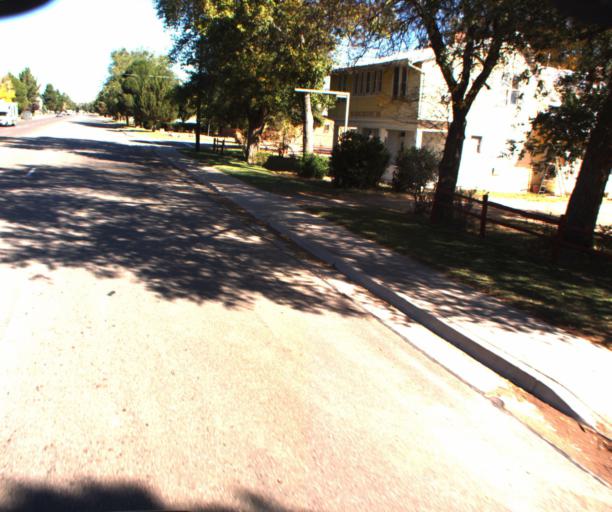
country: US
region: Arizona
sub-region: Coconino County
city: Fredonia
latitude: 36.9468
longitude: -112.5263
